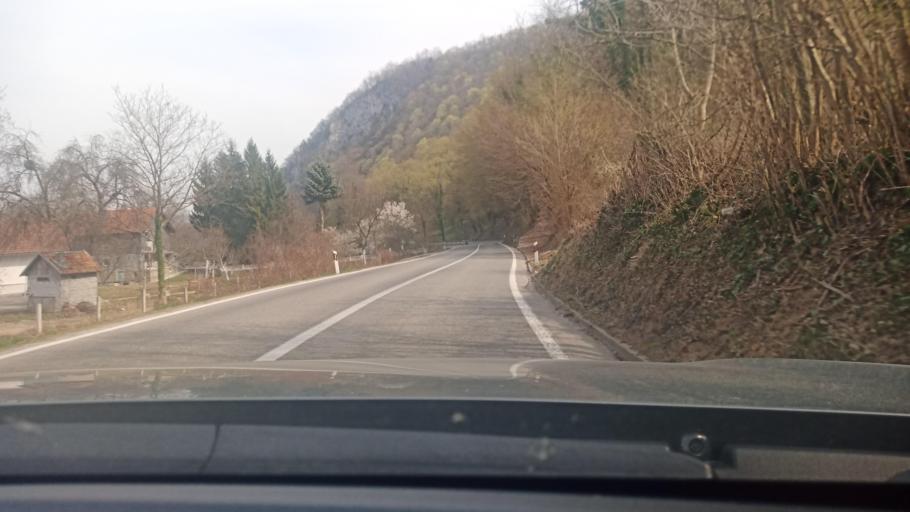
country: BA
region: Federation of Bosnia and Herzegovina
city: Bosanska Krupa
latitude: 44.8776
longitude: 16.1245
